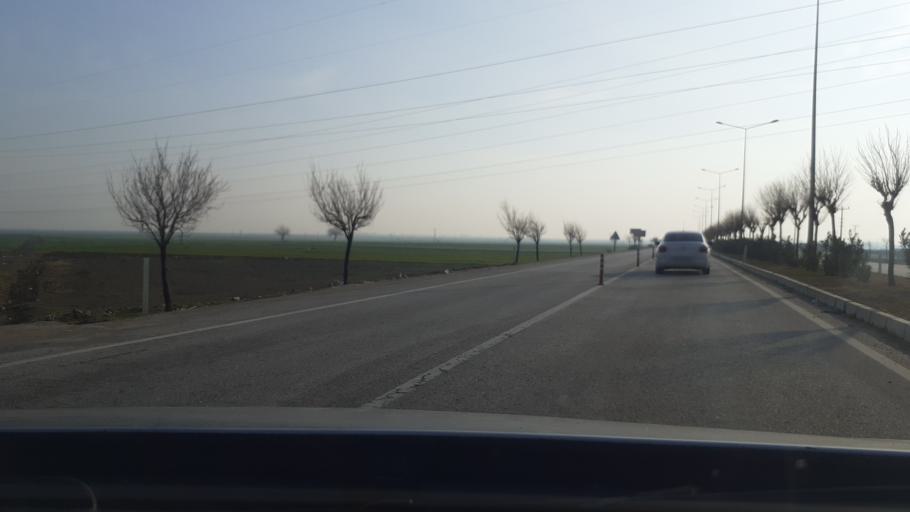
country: TR
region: Hatay
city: Serinyol
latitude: 36.3713
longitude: 36.2448
